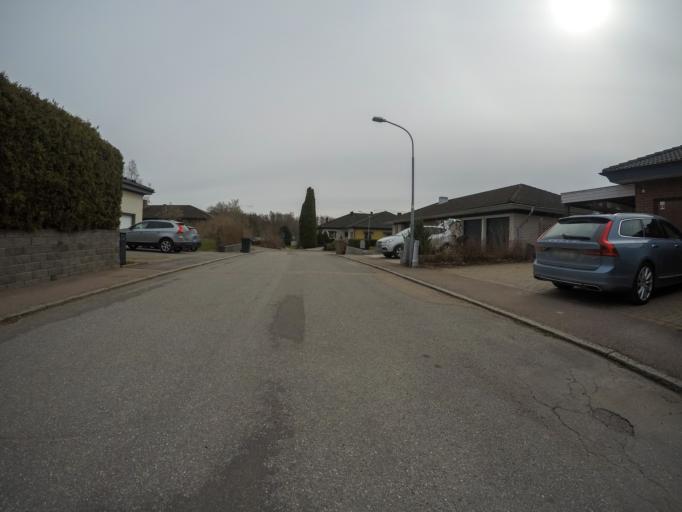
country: SE
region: Vaestmanland
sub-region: Vasteras
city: Vasteras
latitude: 59.5944
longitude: 16.6006
